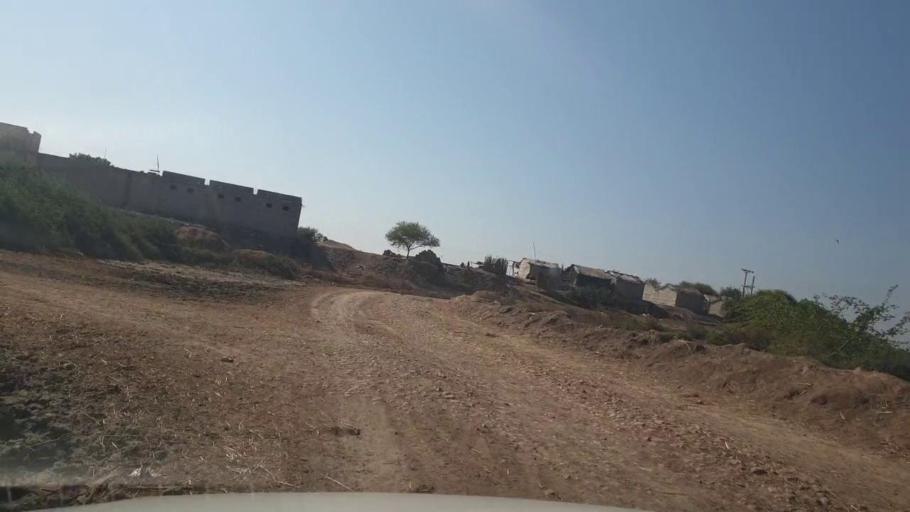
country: PK
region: Sindh
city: Chuhar Jamali
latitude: 24.4402
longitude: 67.8441
